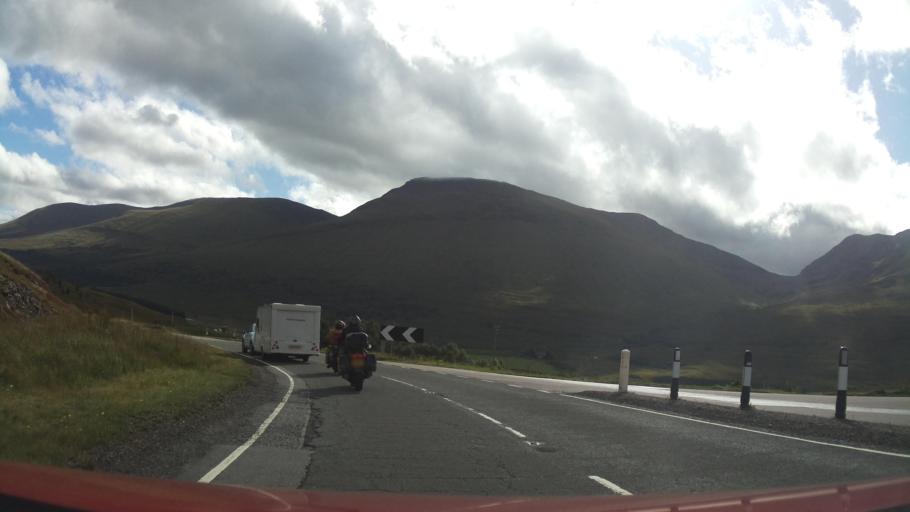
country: GB
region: Scotland
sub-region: Highland
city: Spean Bridge
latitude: 56.5665
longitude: -4.7556
